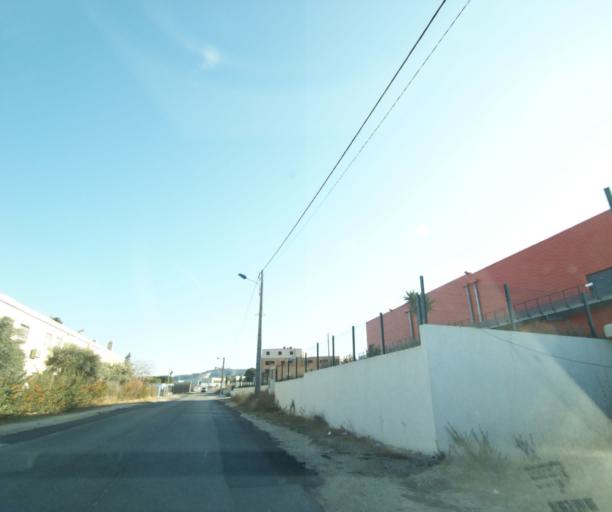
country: FR
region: Provence-Alpes-Cote d'Azur
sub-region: Departement des Bouches-du-Rhone
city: Chateauneuf-les-Martigues
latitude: 43.3960
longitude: 5.1353
